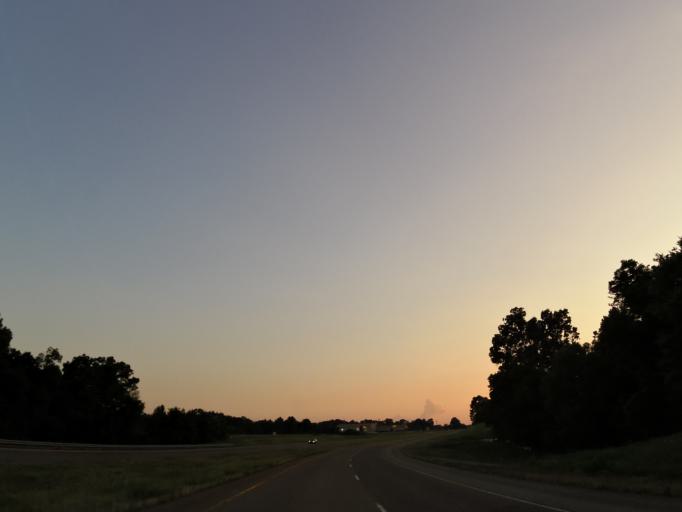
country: US
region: Tennessee
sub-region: Carroll County
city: McKenzie
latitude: 36.1971
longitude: -88.4115
